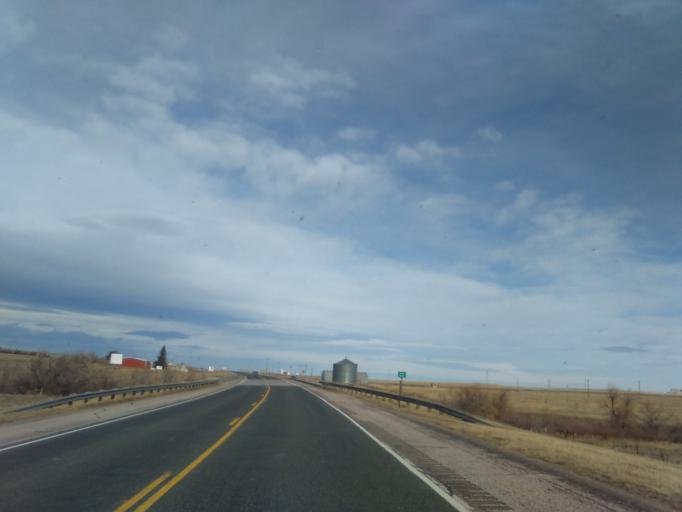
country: US
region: Wyoming
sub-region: Goshen County
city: Torrington
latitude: 41.6406
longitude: -104.2410
